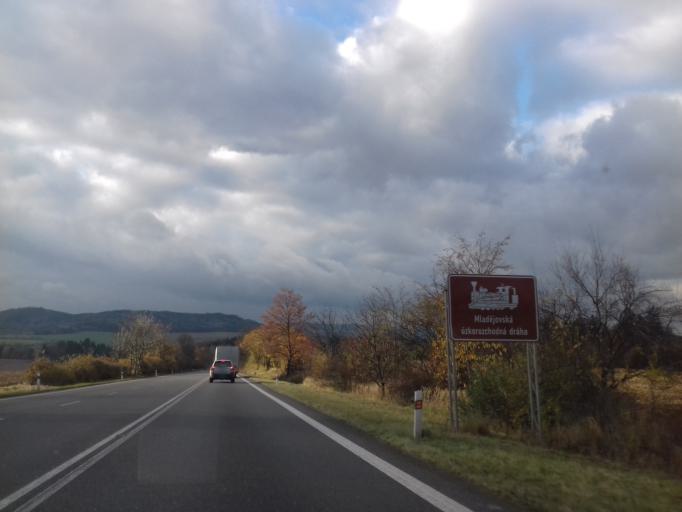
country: CZ
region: Pardubicky
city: Mestecko Trnavka
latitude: 49.7700
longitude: 16.7383
